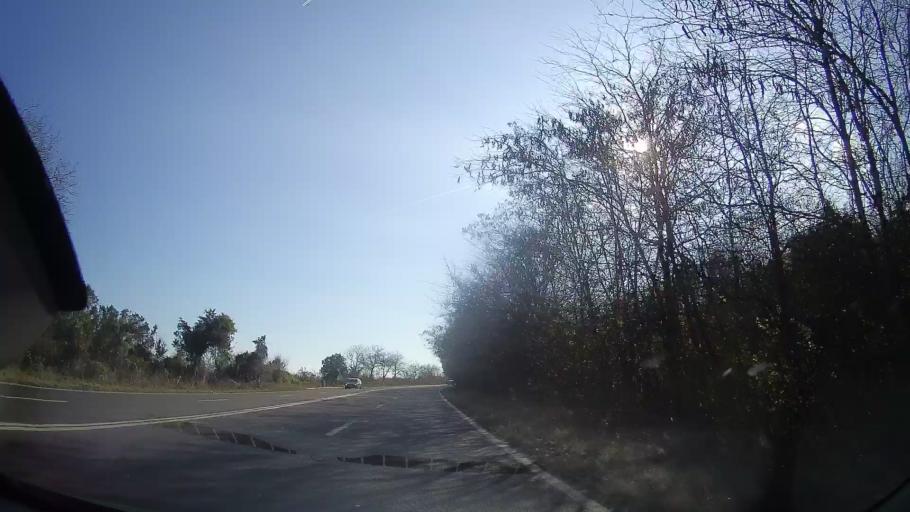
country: RO
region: Constanta
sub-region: Comuna Douazeci si Trei August
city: Dulcesti
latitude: 43.8876
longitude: 28.5730
